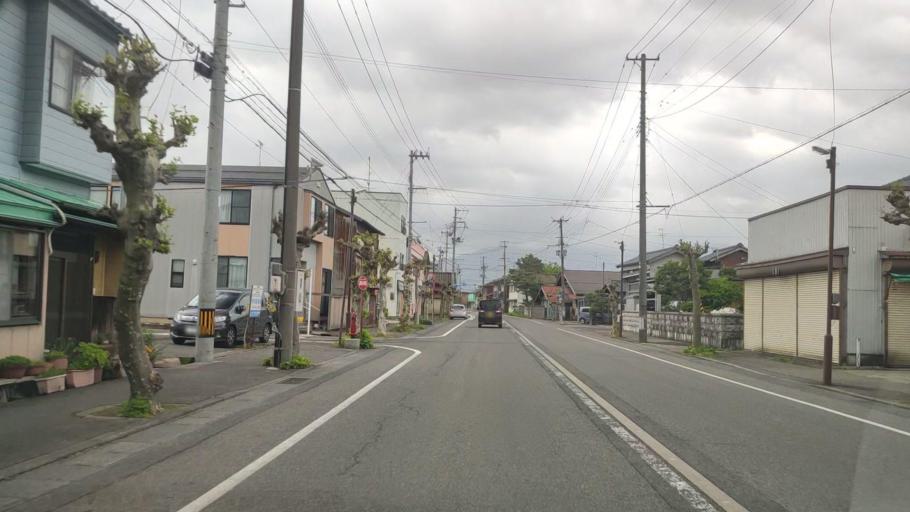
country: JP
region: Niigata
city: Gosen
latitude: 37.7369
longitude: 139.1849
